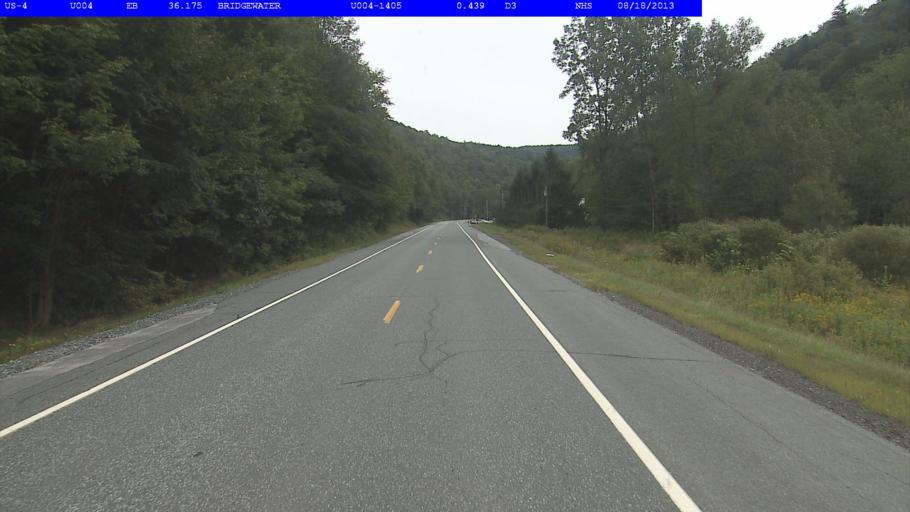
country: US
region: Vermont
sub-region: Windsor County
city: Woodstock
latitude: 43.6020
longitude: -72.7419
